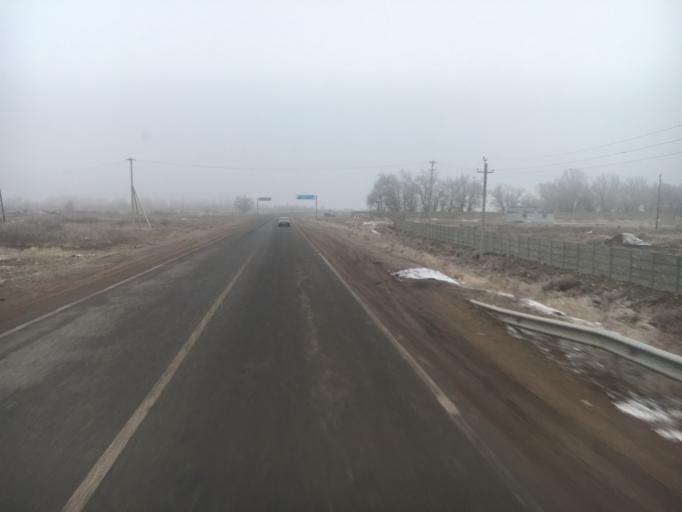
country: KZ
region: Zhambyl
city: Sarykemer
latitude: 43.0403
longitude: 71.5358
